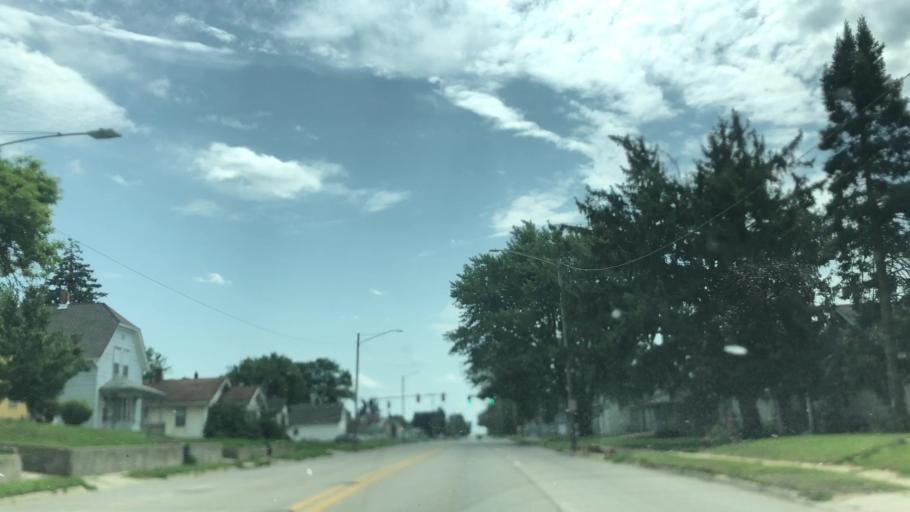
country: US
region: Iowa
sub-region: Marshall County
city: Marshalltown
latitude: 42.0358
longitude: -92.9127
